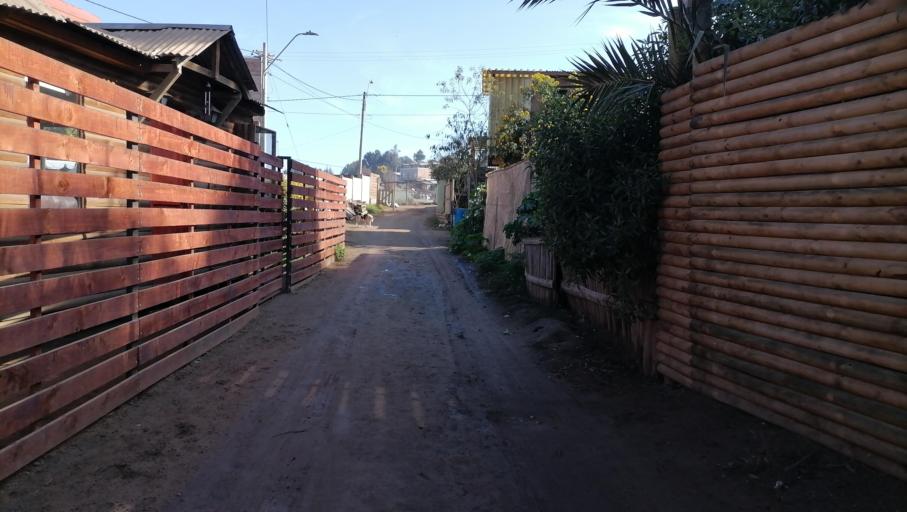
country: CL
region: Valparaiso
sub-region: Provincia de Valparaiso
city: Vina del Mar
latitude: -32.9007
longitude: -71.4947
